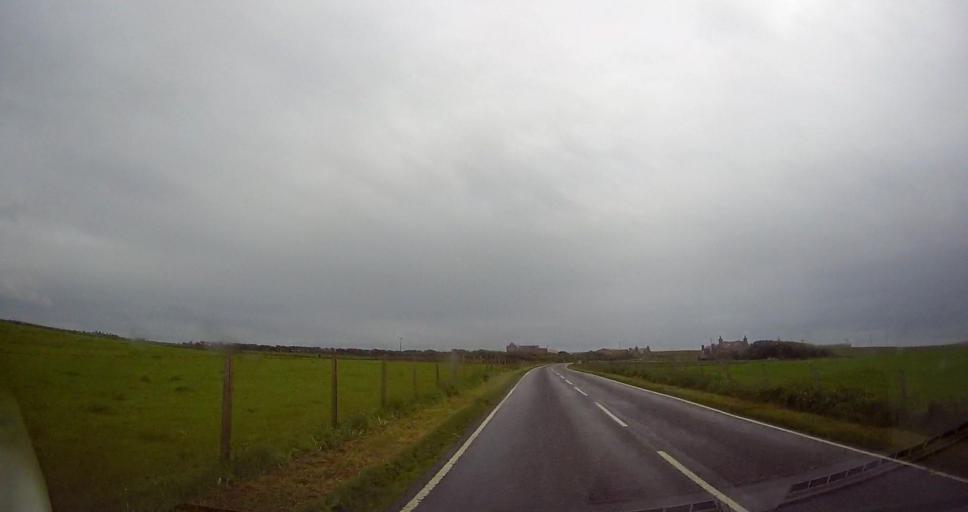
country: GB
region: Scotland
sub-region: Orkney Islands
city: Stromness
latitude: 59.0350
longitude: -3.2825
